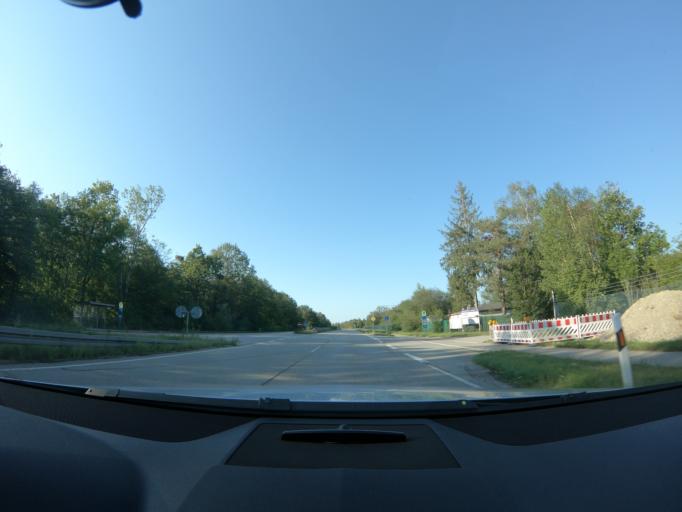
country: DE
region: Bavaria
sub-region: Upper Bavaria
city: Oberschleissheim
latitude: 48.2417
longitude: 11.6012
